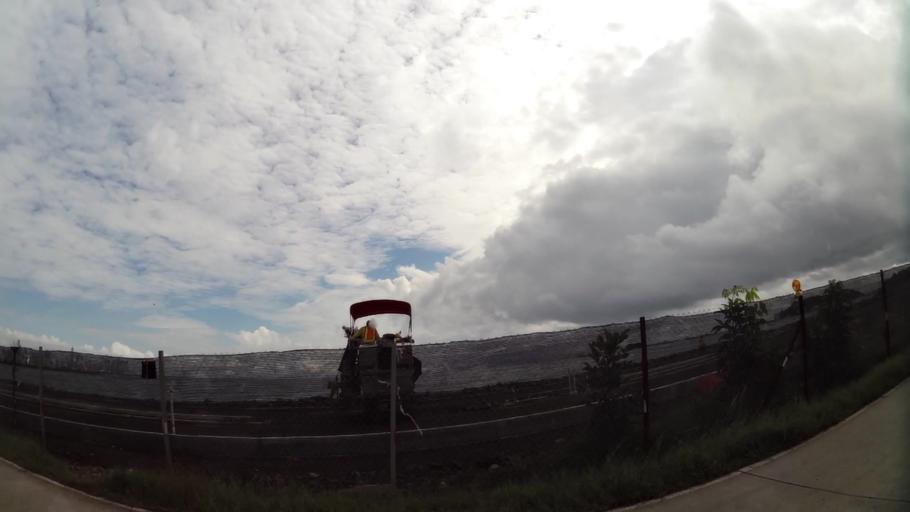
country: PA
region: Panama
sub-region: Distrito de Panama
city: Ancon
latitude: 8.9300
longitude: -79.5438
